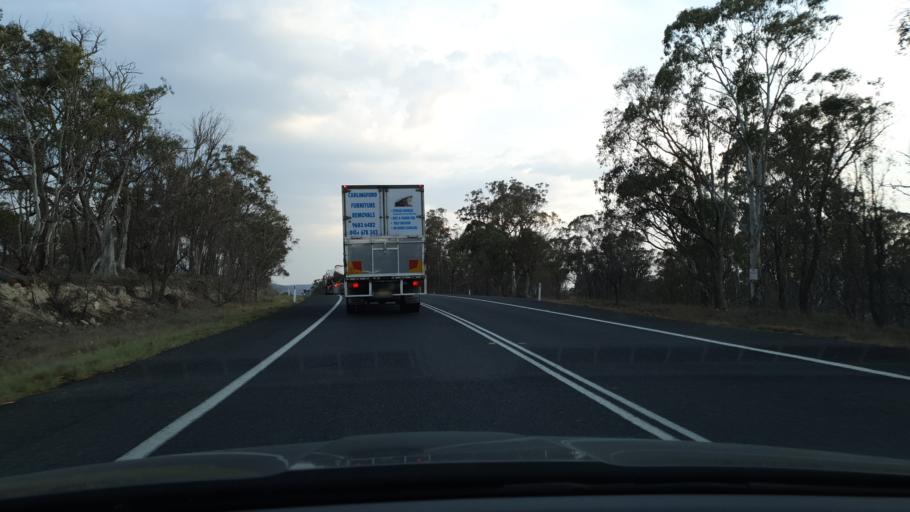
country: AU
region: New South Wales
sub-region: Glen Innes Severn
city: Glen Innes
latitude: -29.5902
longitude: 151.8706
